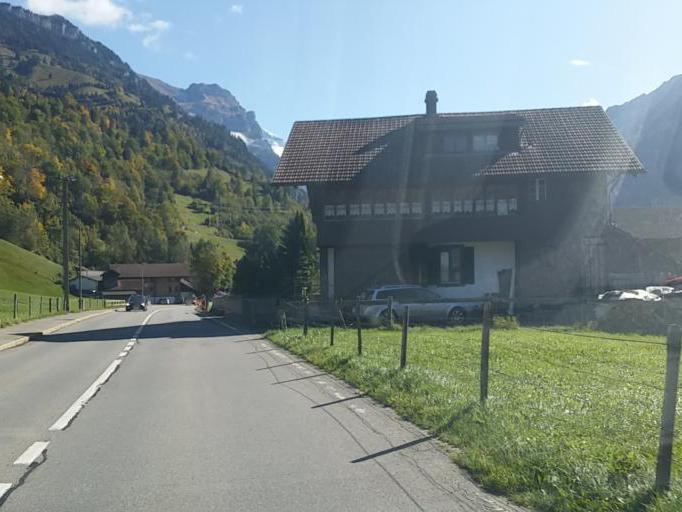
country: CH
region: Bern
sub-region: Frutigen-Niedersimmental District
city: Frutigen
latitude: 46.5599
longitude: 7.6591
